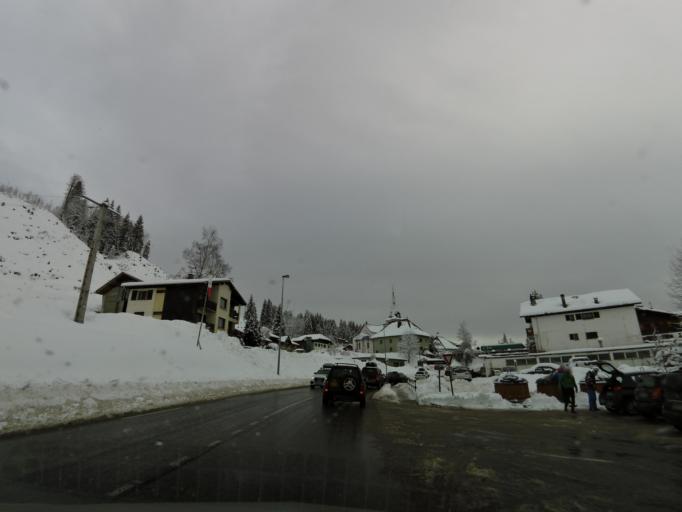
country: FR
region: Rhone-Alpes
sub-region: Departement de la Haute-Savoie
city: Les Gets
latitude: 46.1622
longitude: 6.6733
